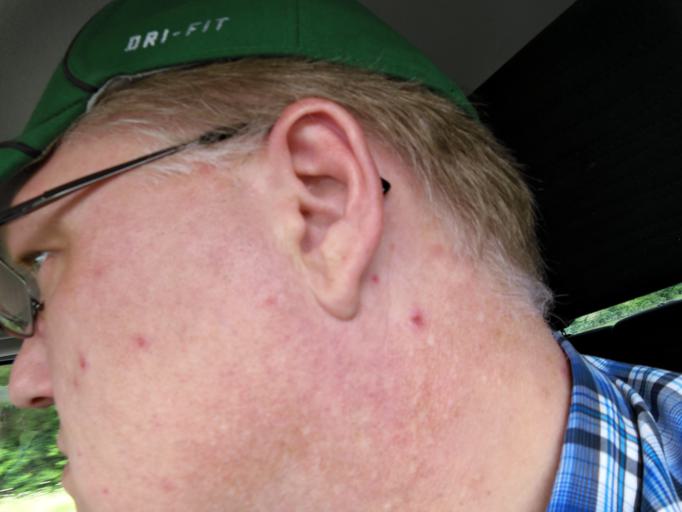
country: US
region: Kentucky
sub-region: Grayson County
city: Leitchfield
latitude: 37.5504
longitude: -86.1144
